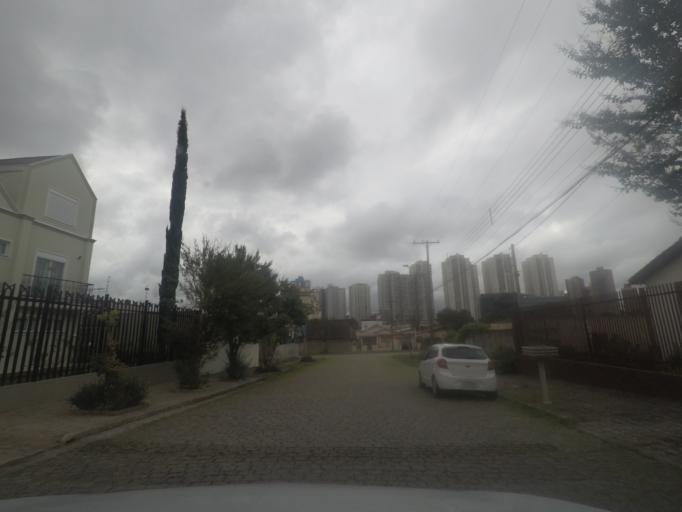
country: BR
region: Parana
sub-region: Curitiba
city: Curitiba
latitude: -25.4406
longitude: -49.2432
